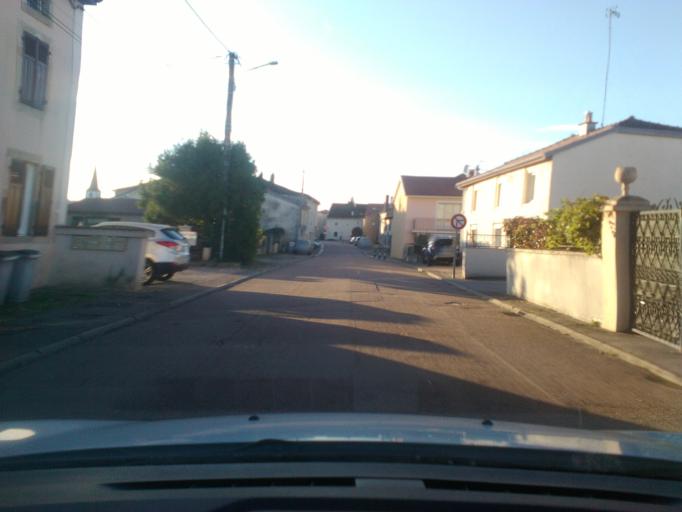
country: FR
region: Lorraine
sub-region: Departement des Vosges
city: Vincey
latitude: 48.3373
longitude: 6.3341
